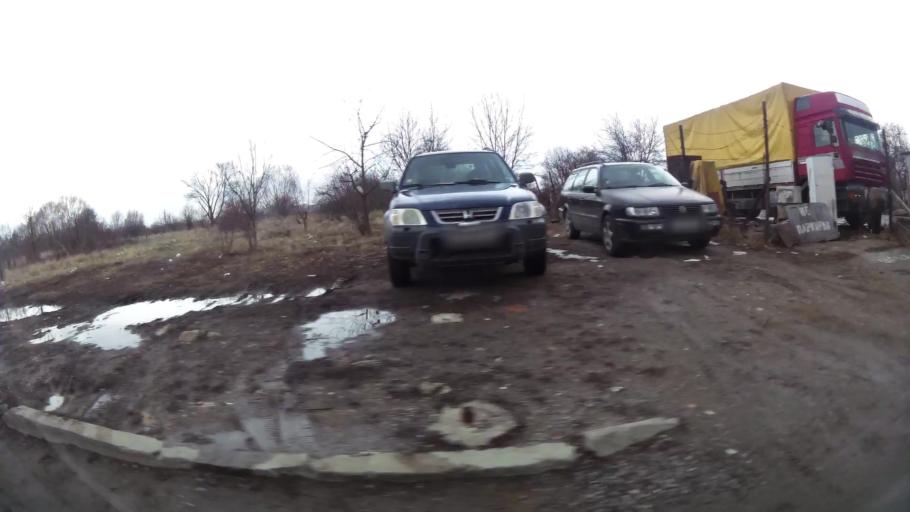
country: BG
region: Sofia-Capital
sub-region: Stolichna Obshtina
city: Sofia
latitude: 42.7372
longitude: 23.2855
